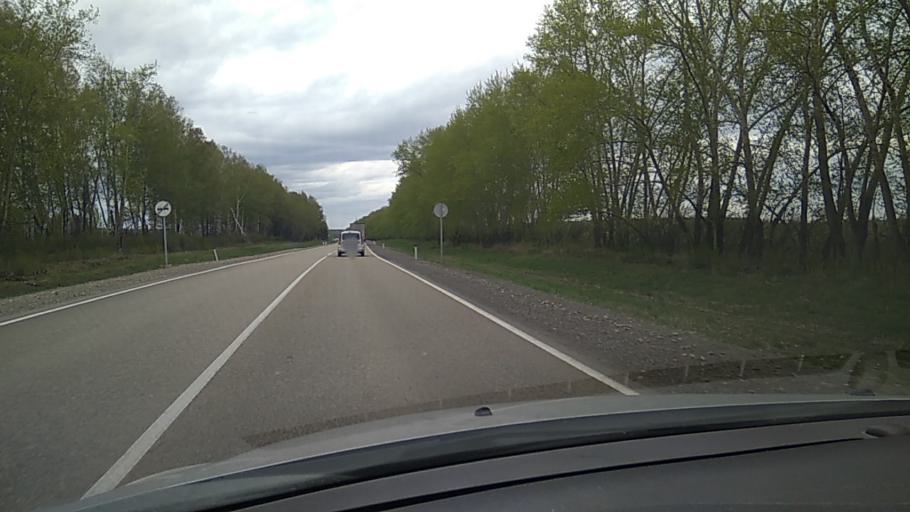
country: RU
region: Sverdlovsk
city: Dvurechensk
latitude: 56.6493
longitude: 61.2023
